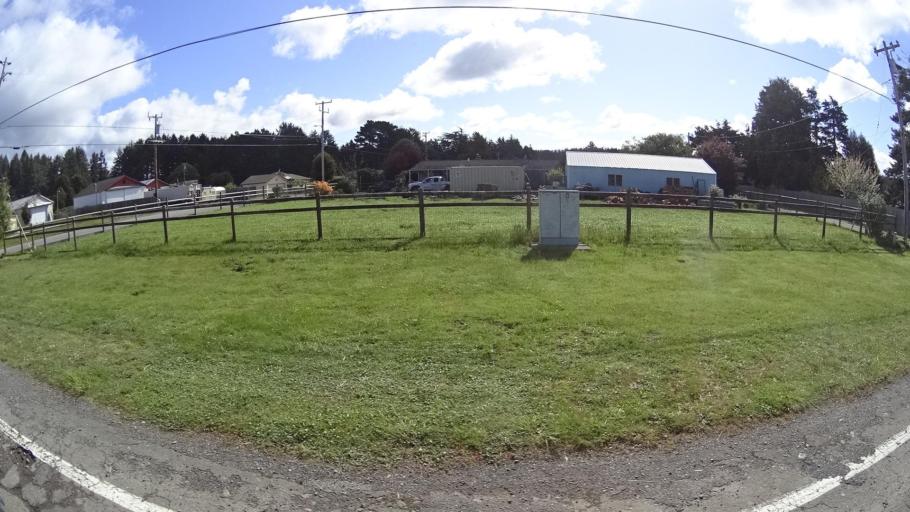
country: US
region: California
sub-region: Humboldt County
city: McKinleyville
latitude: 40.9794
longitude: -124.1009
